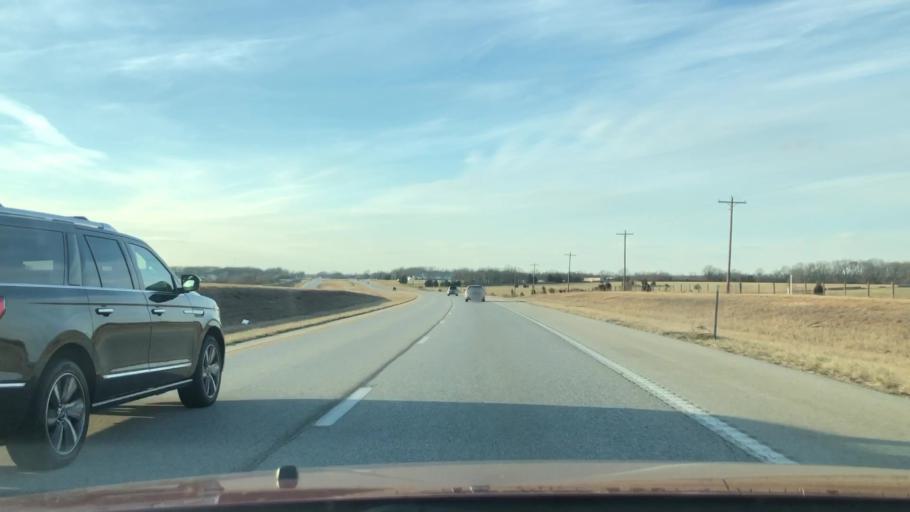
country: US
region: Missouri
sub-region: Webster County
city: Seymour
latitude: 37.1233
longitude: -92.7003
